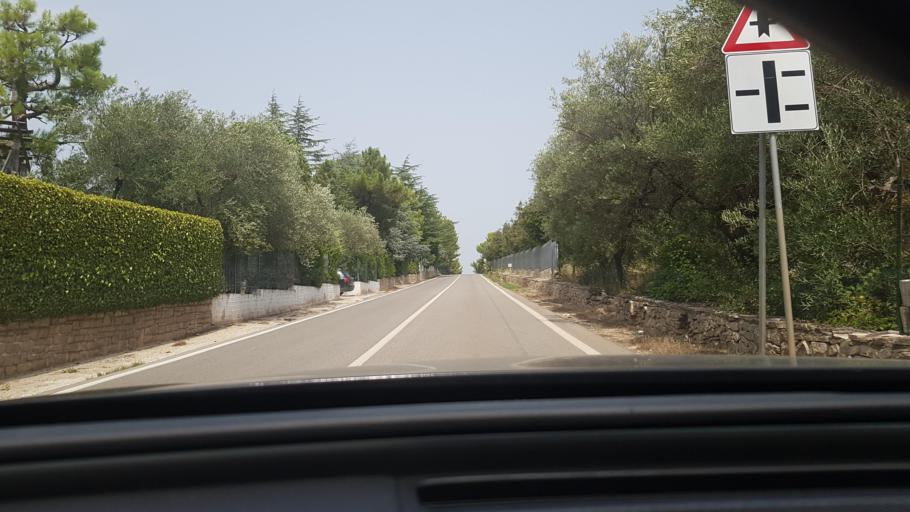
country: IT
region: Apulia
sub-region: Provincia di Barletta - Andria - Trani
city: Andria
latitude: 41.1208
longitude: 16.2852
